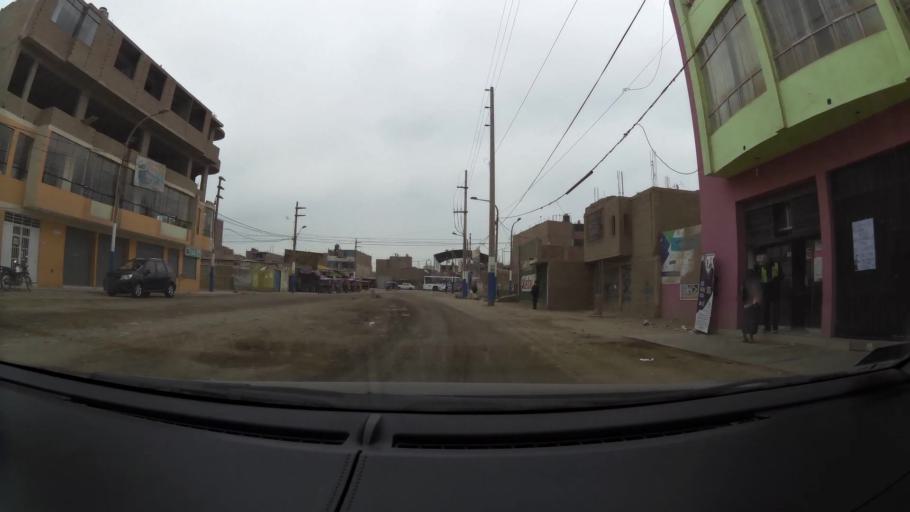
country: PE
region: Lima
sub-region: Lima
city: Independencia
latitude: -11.9598
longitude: -77.0977
